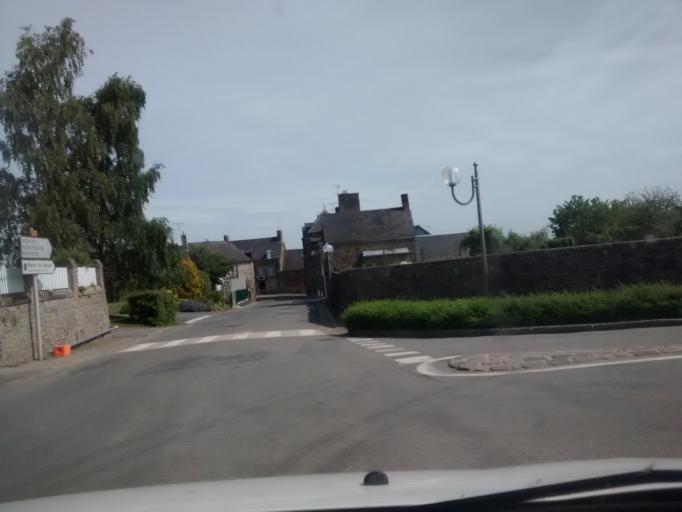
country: FR
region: Lower Normandy
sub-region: Departement de la Manche
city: Pontorson
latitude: 48.5088
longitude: -1.5236
